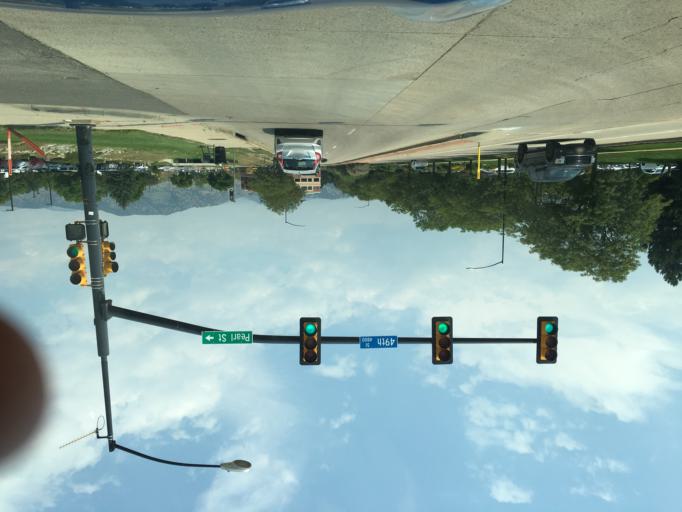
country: US
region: Colorado
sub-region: Boulder County
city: Boulder
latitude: 40.0221
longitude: -105.2382
